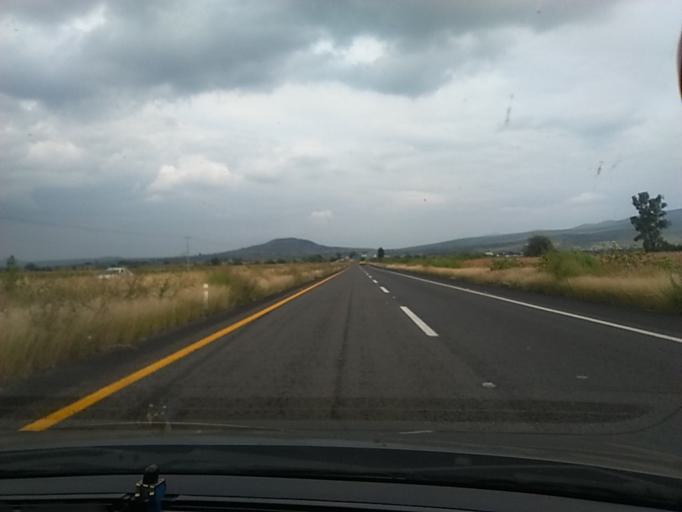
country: MX
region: Michoacan
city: Ecuandureo
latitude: 20.1751
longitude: -102.2136
